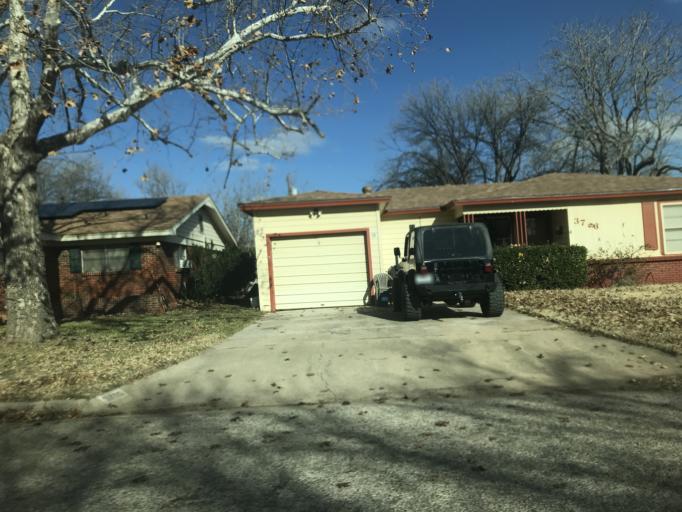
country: US
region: Texas
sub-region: Taylor County
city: Abilene
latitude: 32.4618
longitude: -99.7707
